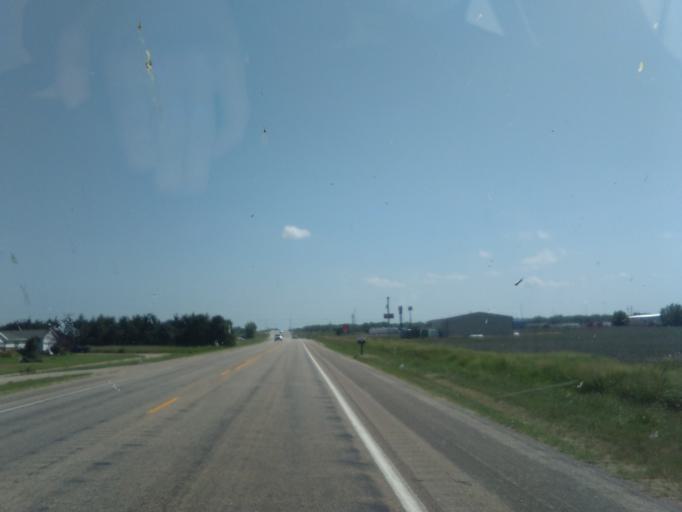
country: US
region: Nebraska
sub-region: Phelps County
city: Holdrege
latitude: 40.6968
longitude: -99.3797
